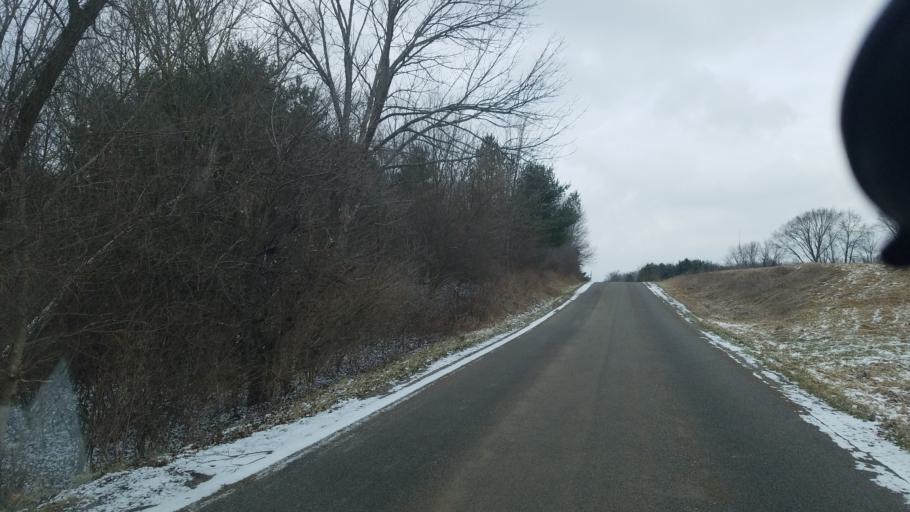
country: US
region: Ohio
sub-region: Morrow County
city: Mount Gilead
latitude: 40.5996
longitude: -82.7938
